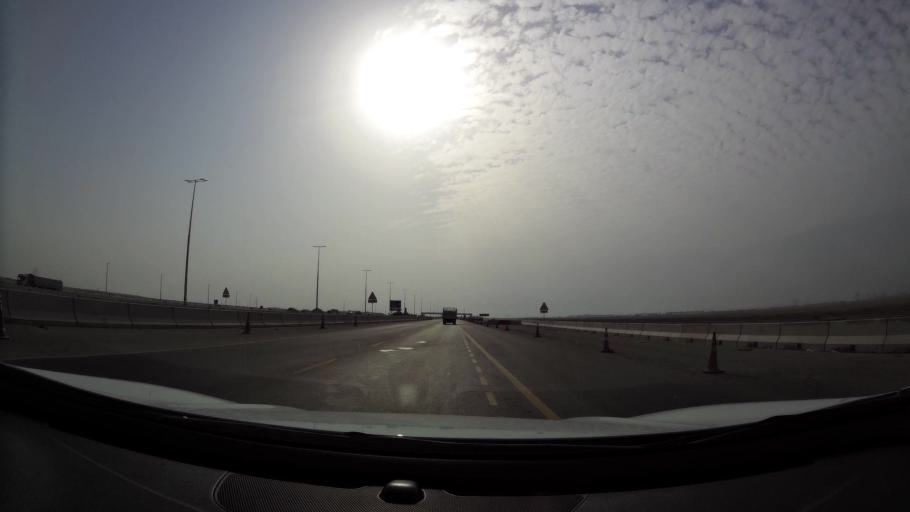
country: AE
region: Abu Dhabi
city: Abu Dhabi
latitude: 24.2818
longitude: 54.5337
